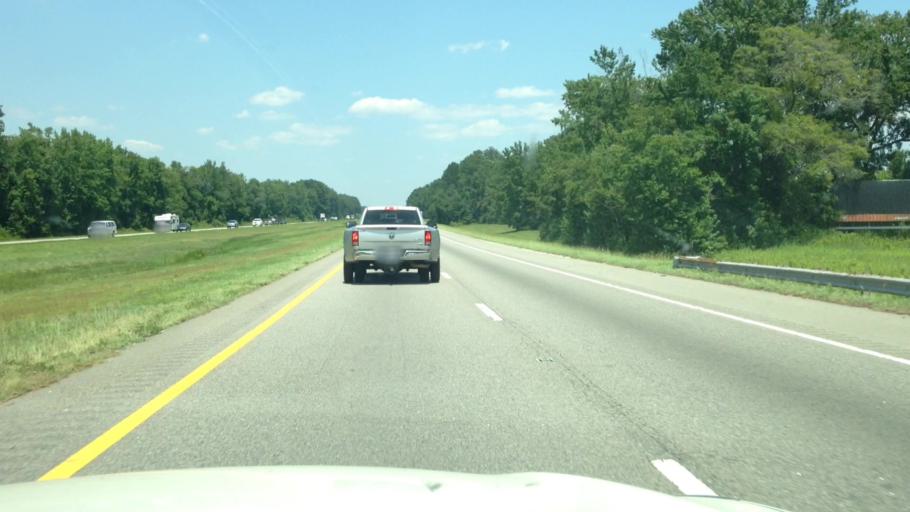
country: US
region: North Carolina
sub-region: Robeson County
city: Fairmont
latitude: 34.5621
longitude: -79.1773
